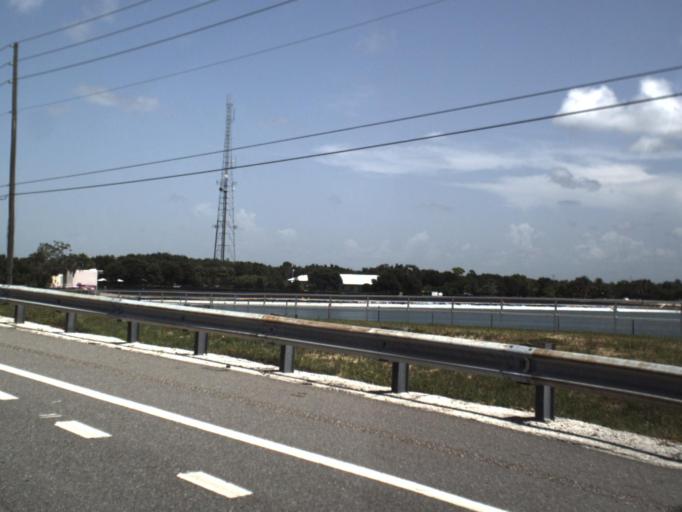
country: US
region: Florida
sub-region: Pinellas County
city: Palm Harbor
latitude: 28.1083
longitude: -82.7683
